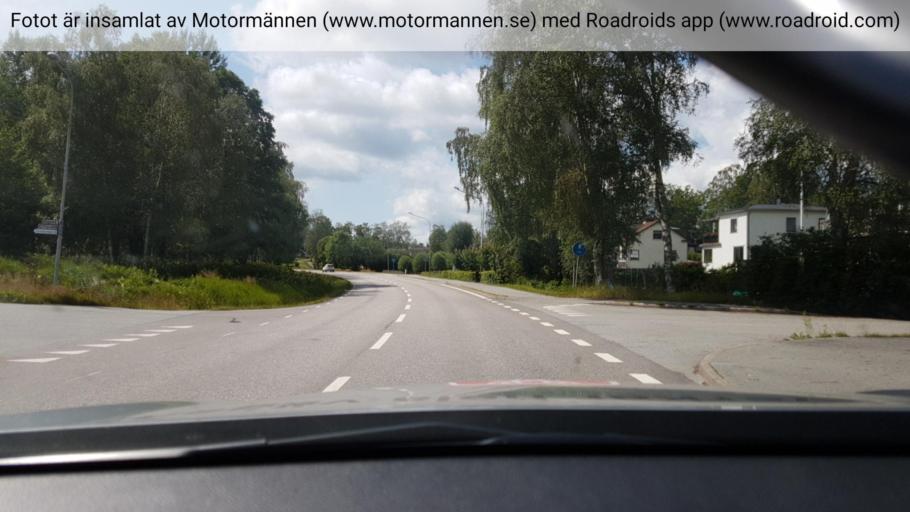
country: SE
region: Vaestra Goetaland
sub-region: Svenljunga Kommun
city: Svenljunga
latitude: 57.4997
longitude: 13.1027
